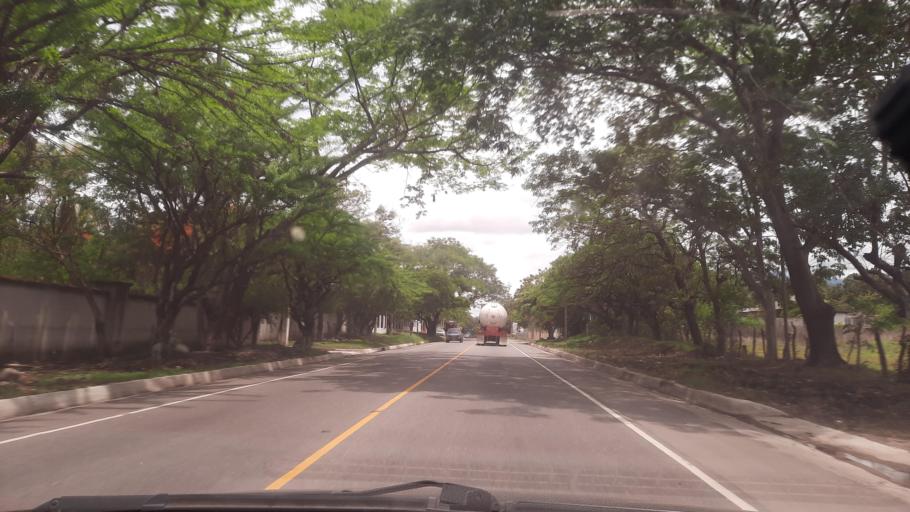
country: GT
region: Zacapa
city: Rio Hondo
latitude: 15.0859
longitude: -89.4706
